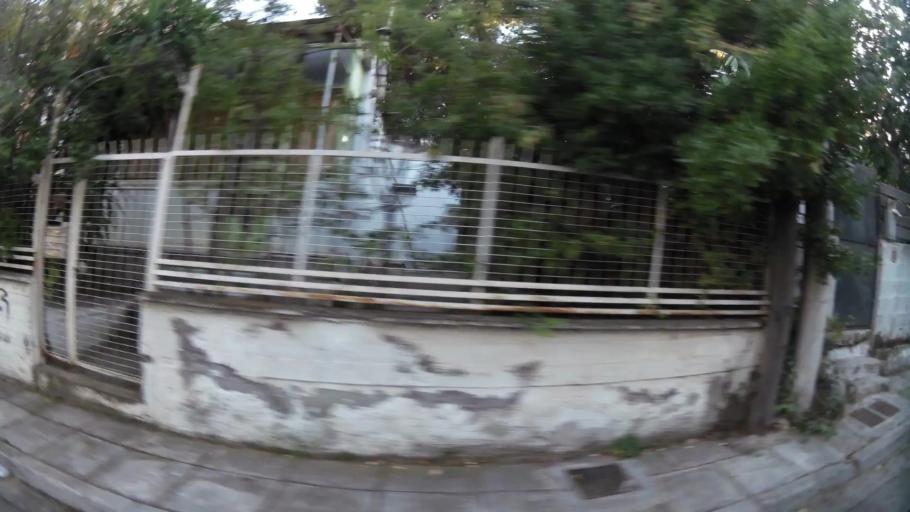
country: GR
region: Attica
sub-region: Nomarchia Athinas
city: Lykovrysi
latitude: 38.0651
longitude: 23.7827
